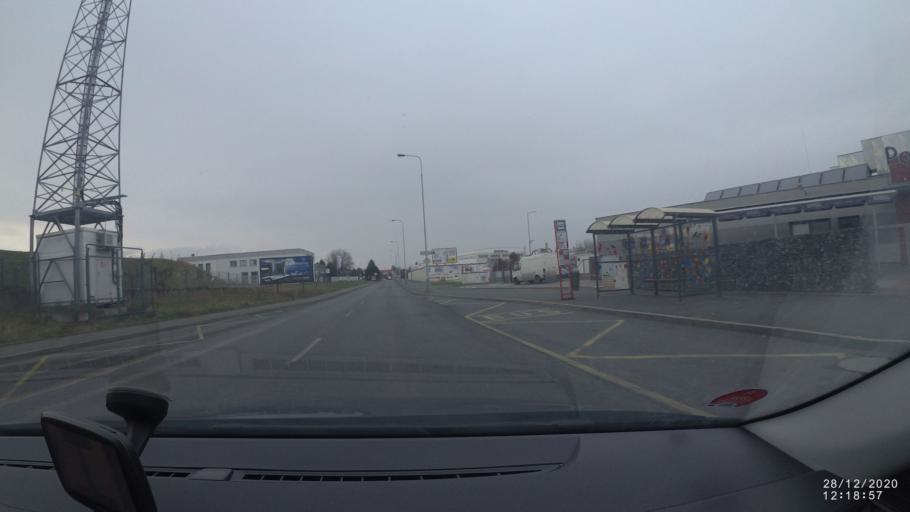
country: CZ
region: Central Bohemia
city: Brandys nad Labem-Stara Boleslav
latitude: 50.1762
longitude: 14.6588
